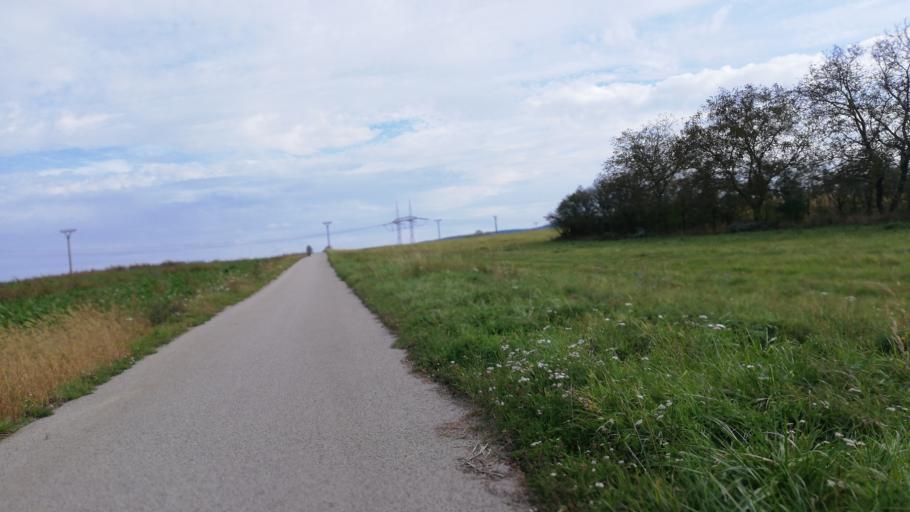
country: CZ
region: South Moravian
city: Sudomerice
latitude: 48.8497
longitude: 17.2562
